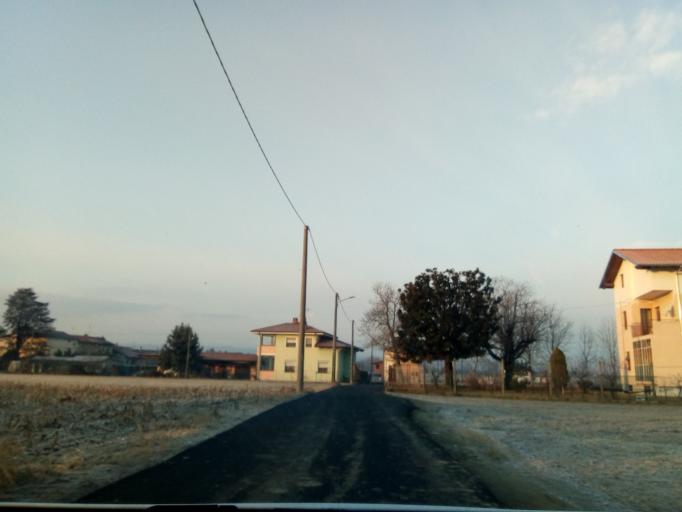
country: IT
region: Piedmont
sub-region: Provincia di Torino
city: Pavone Canavese
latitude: 45.4298
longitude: 7.8783
